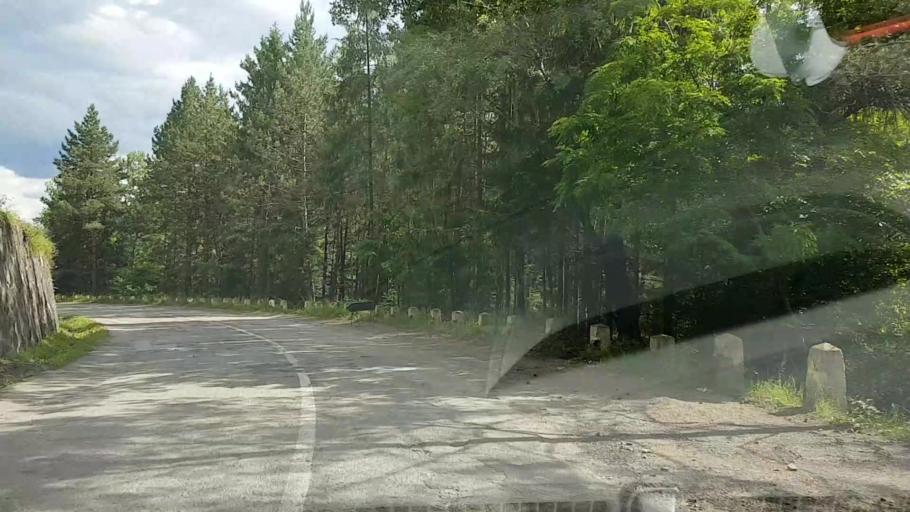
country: RO
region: Neamt
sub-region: Comuna Hangu
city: Hangu
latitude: 47.0500
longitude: 26.0083
